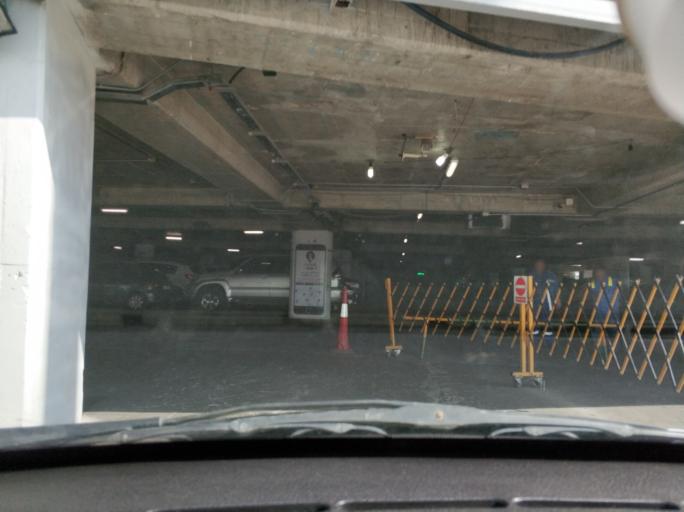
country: IR
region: Tehran
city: Tehran
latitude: 35.6928
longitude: 51.3218
